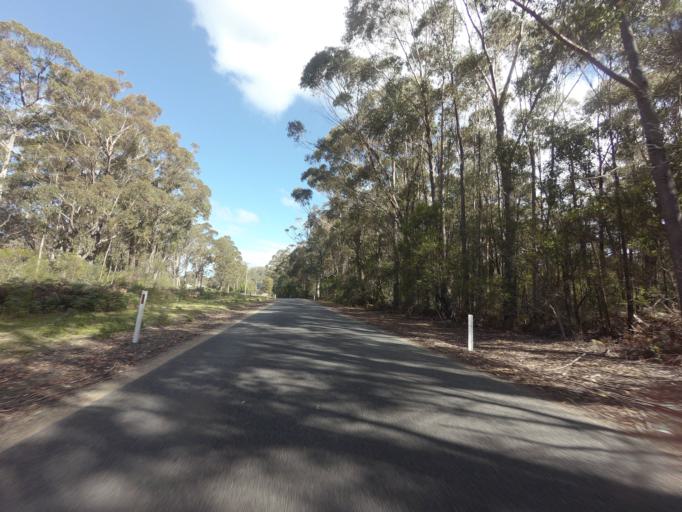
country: AU
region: Tasmania
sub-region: Break O'Day
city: St Helens
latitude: -41.6419
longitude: 148.2428
